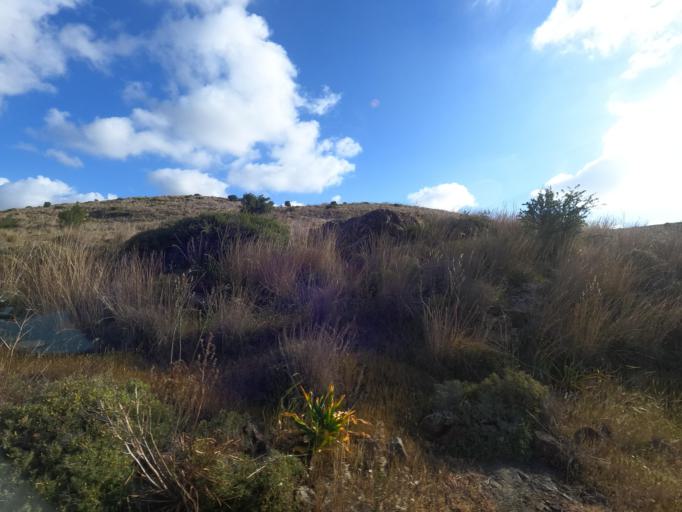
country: CY
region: Lefkosia
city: Peristerona
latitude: 35.0671
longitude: 33.0479
